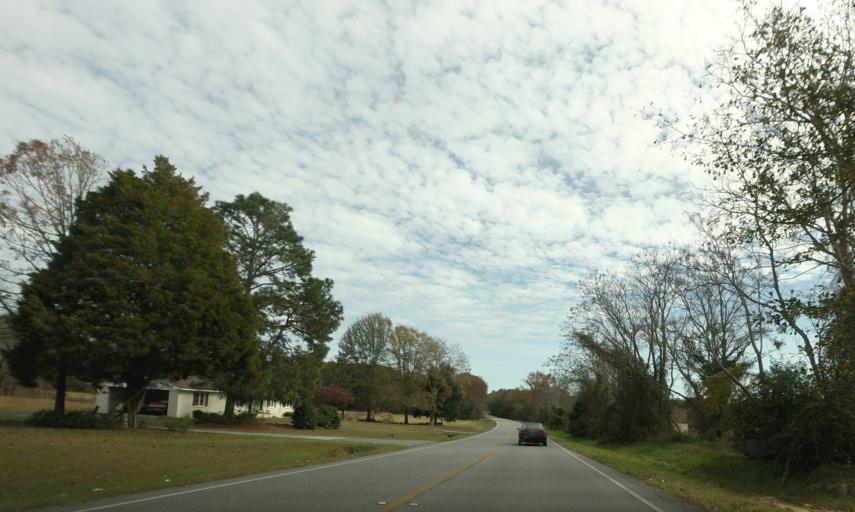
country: US
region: Georgia
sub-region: Dodge County
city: Chester
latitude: 32.4101
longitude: -83.2431
